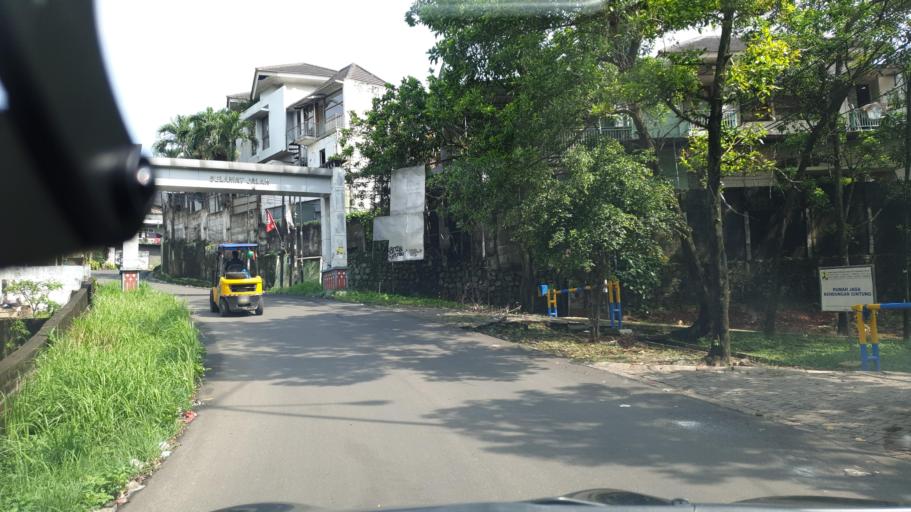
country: ID
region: Banten
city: South Tangerang
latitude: -6.3006
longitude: 106.7640
